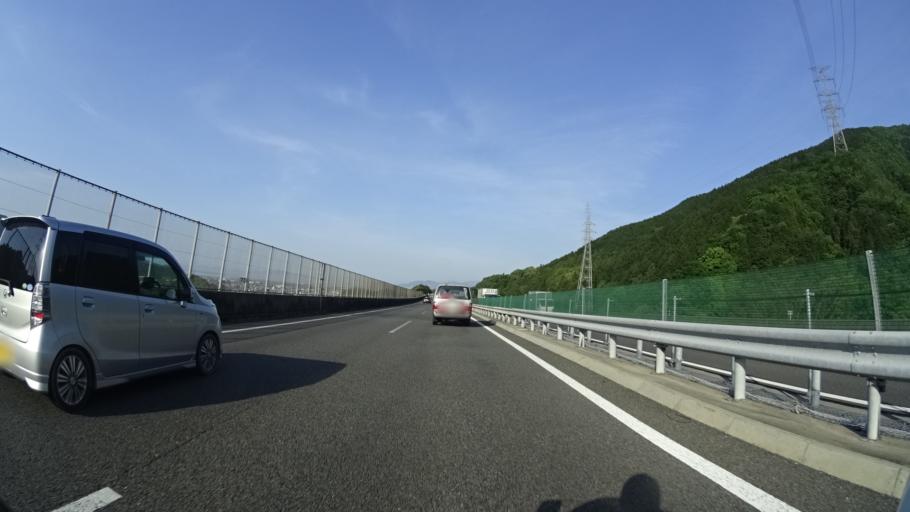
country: JP
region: Ehime
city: Niihama
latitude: 33.9430
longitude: 133.4012
